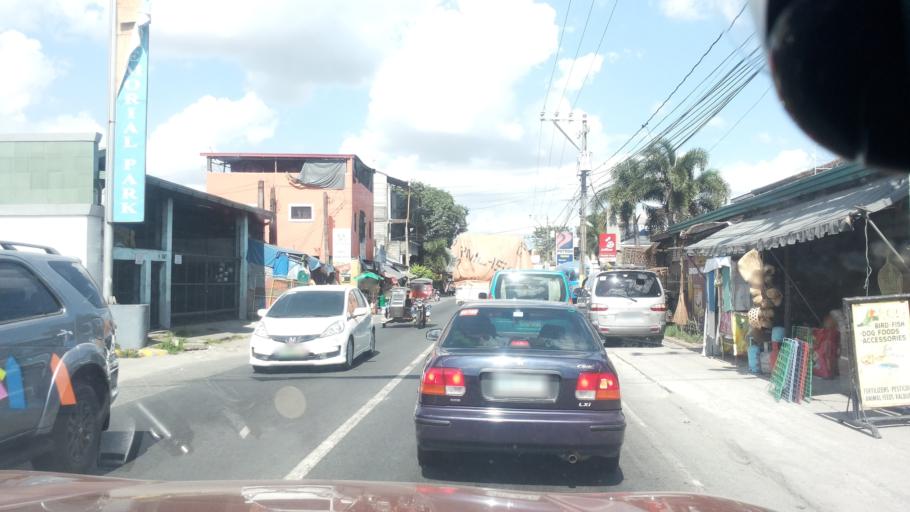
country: PH
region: Central Luzon
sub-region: Province of Bulacan
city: Plaridel
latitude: 14.8659
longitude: 120.8599
